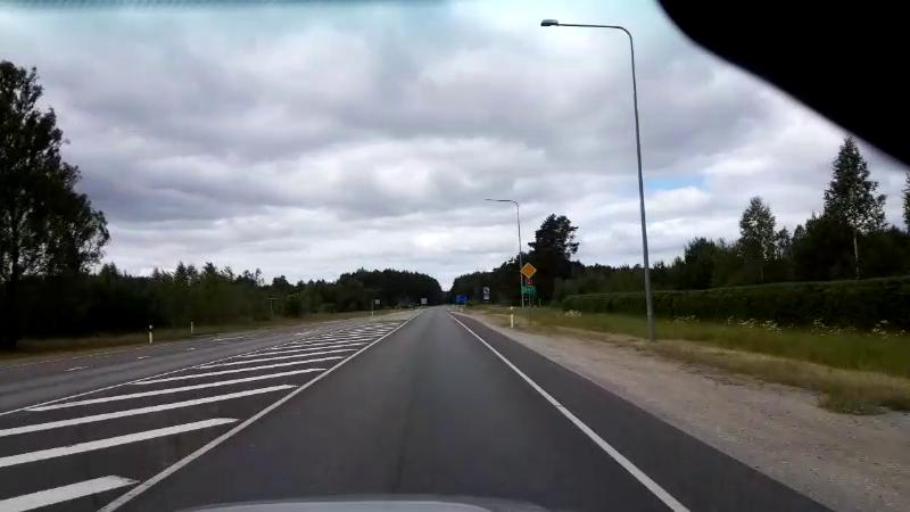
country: EE
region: Paernumaa
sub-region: Paikuse vald
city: Paikuse
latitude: 58.2895
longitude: 24.5907
